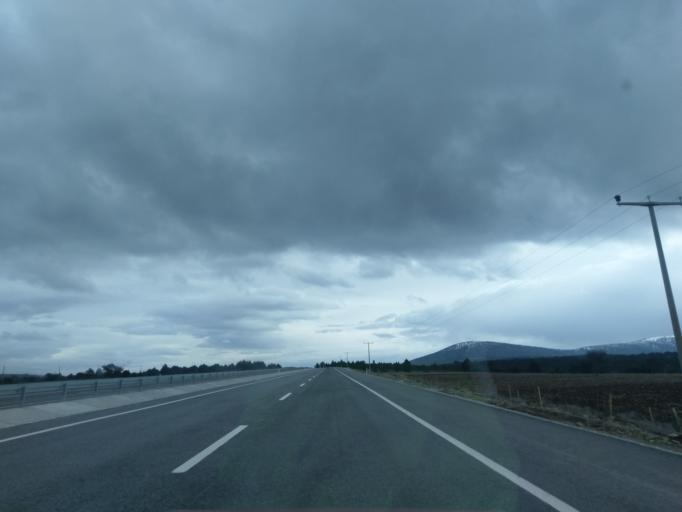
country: TR
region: Kuetahya
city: Cavdarhisar
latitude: 39.2238
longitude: 29.7278
